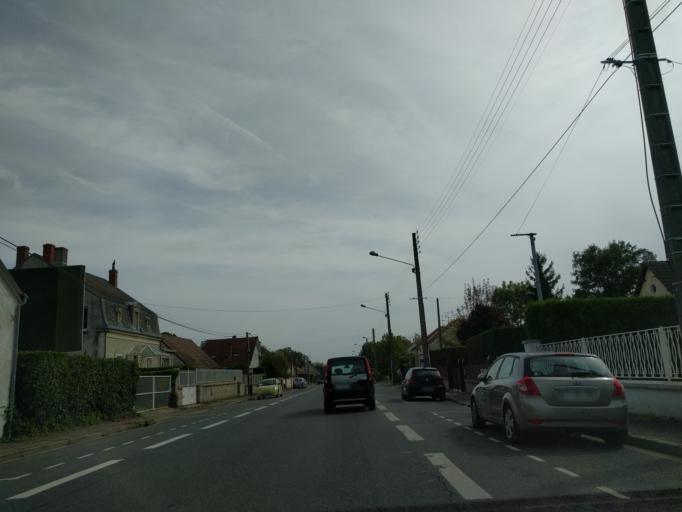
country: FR
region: Centre
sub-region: Departement du Cher
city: Bourges
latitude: 47.0621
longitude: 2.4226
